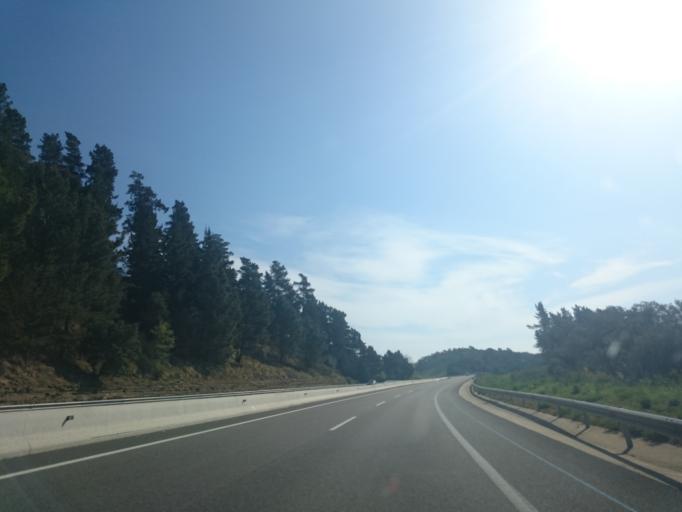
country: ES
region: Catalonia
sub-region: Provincia de Girona
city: Santa Coloma de Farners
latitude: 41.8758
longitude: 2.6329
